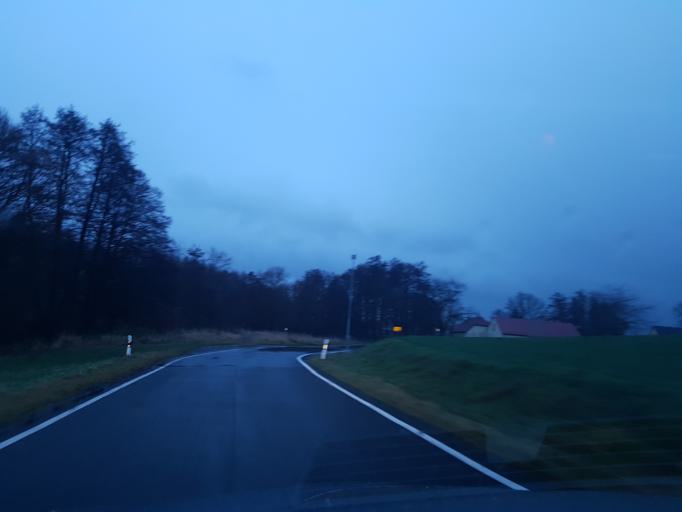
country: DE
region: Saxony
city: Priestewitz
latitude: 51.2350
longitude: 13.5354
